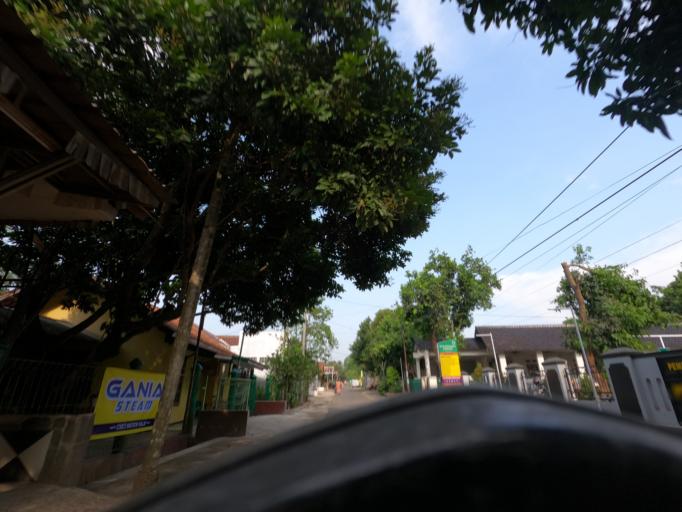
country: ID
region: West Java
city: Lembang
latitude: -6.5795
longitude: 107.7657
